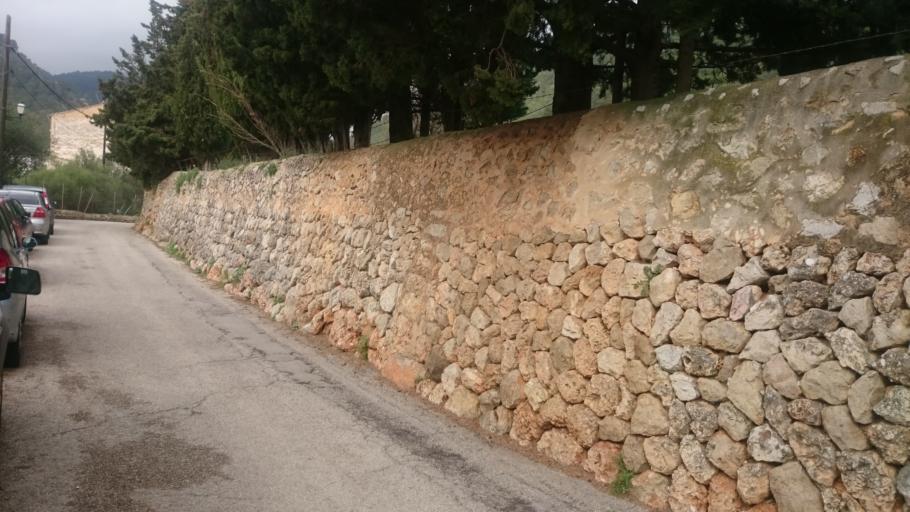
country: ES
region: Balearic Islands
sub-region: Illes Balears
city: Alaro
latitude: 39.7068
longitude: 2.7854
